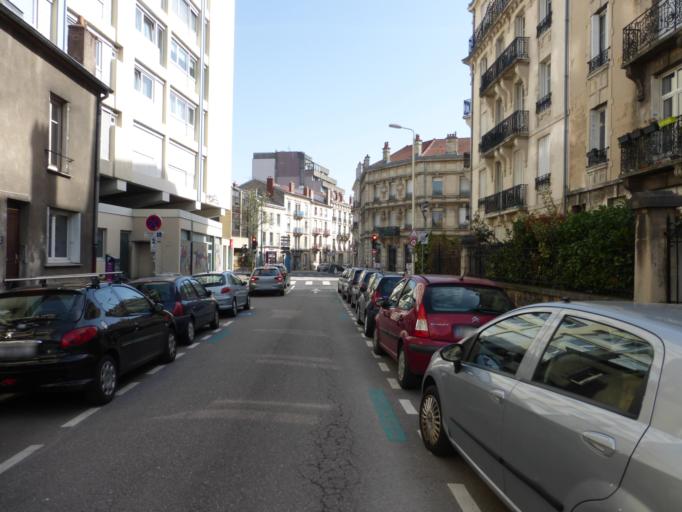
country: FR
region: Lorraine
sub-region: Departement de Meurthe-et-Moselle
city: Nancy
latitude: 48.6837
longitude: 6.1763
